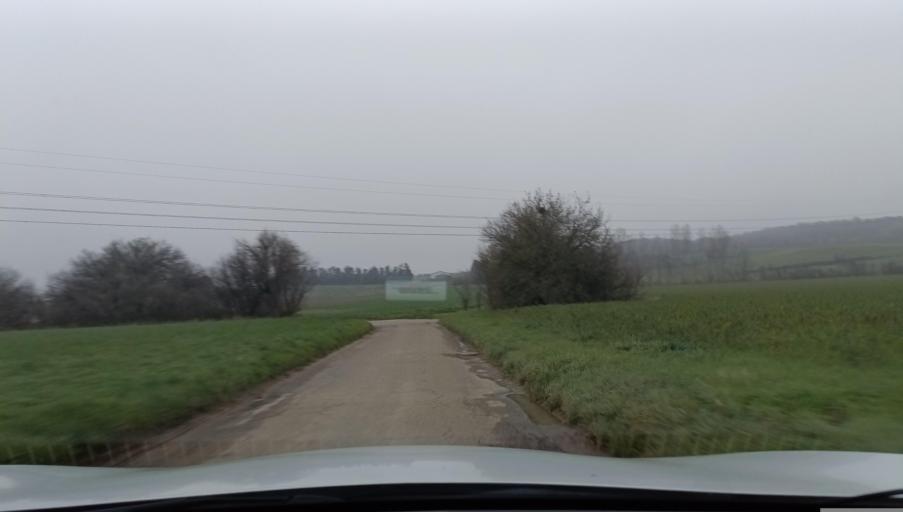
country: FR
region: Rhone-Alpes
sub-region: Departement de l'Isere
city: Seyssuel
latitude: 45.5793
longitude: 4.8491
